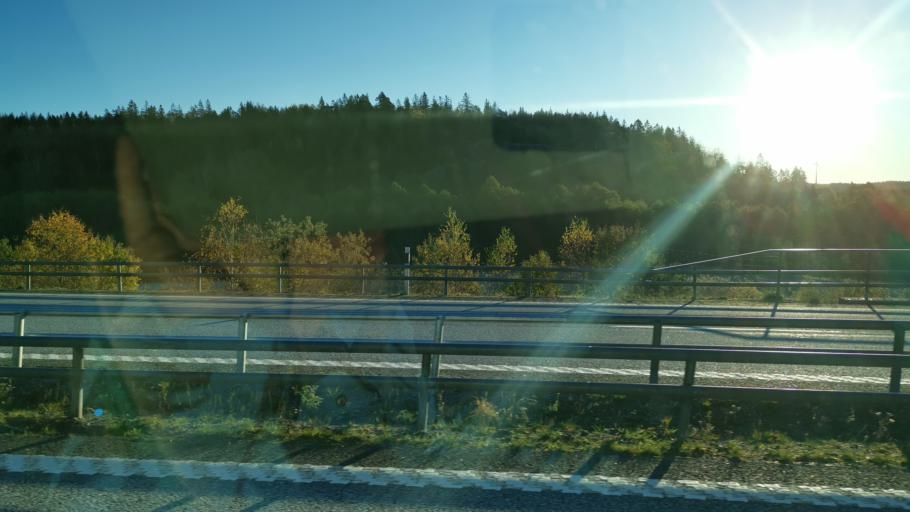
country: SE
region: Vaestra Goetaland
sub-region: Tanums Kommun
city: Tanumshede
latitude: 58.5846
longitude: 11.4516
